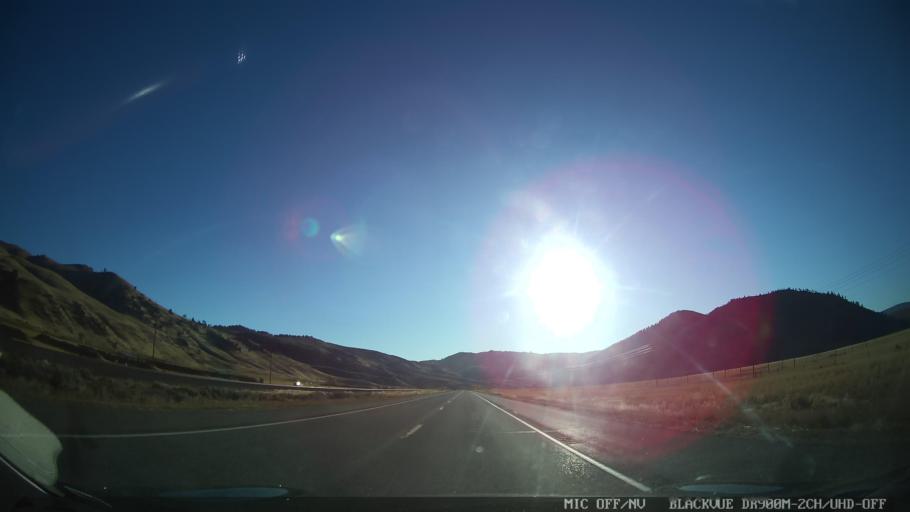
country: US
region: Colorado
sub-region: Grand County
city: Hot Sulphur Springs
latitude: 40.0520
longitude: -106.1489
